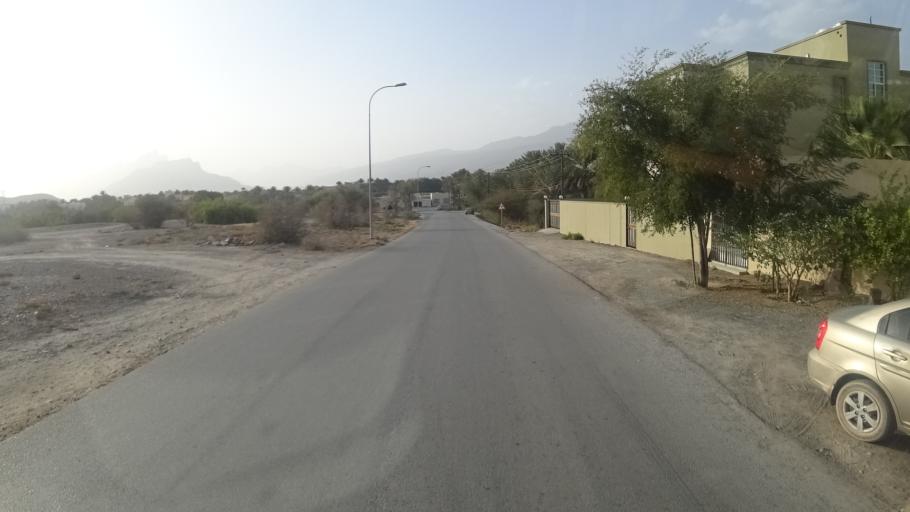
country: OM
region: Muhafazat ad Dakhiliyah
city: Bahla'
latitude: 23.0939
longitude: 57.3103
